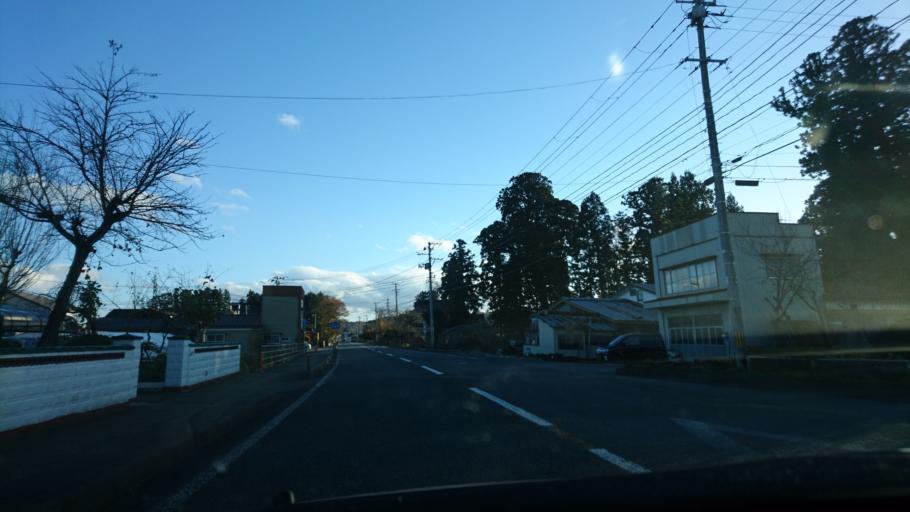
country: JP
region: Iwate
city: Ichinoseki
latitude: 38.9778
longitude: 141.1165
